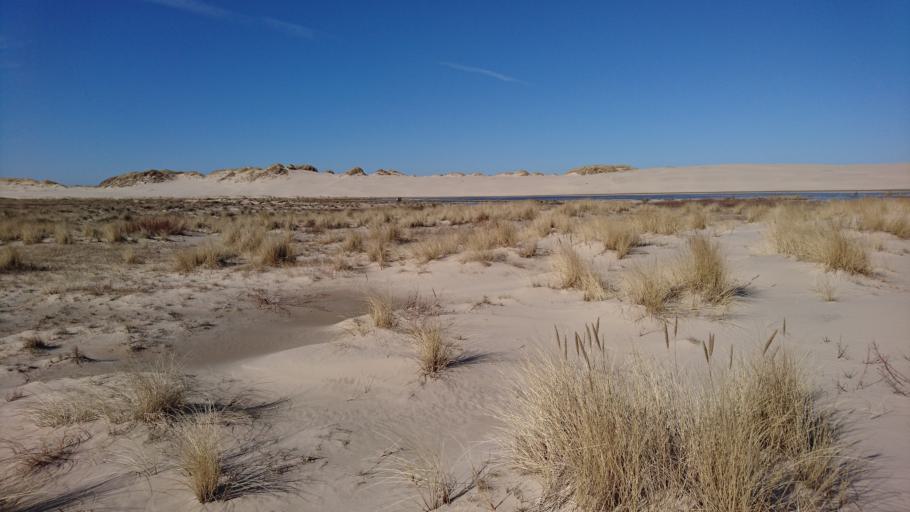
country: DK
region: North Denmark
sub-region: Frederikshavn Kommune
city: Strandby
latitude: 57.6484
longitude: 10.4034
